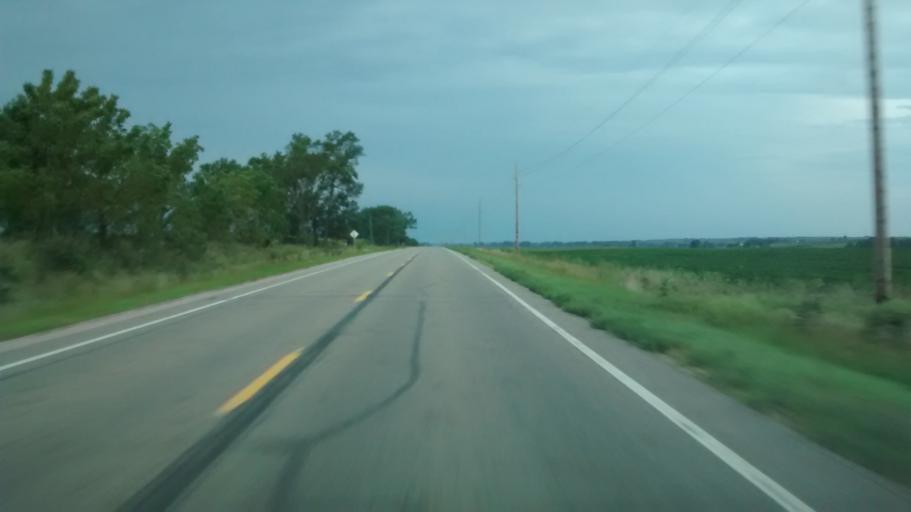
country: US
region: Iowa
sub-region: Plymouth County
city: Kingsley
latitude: 42.5600
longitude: -96.0118
